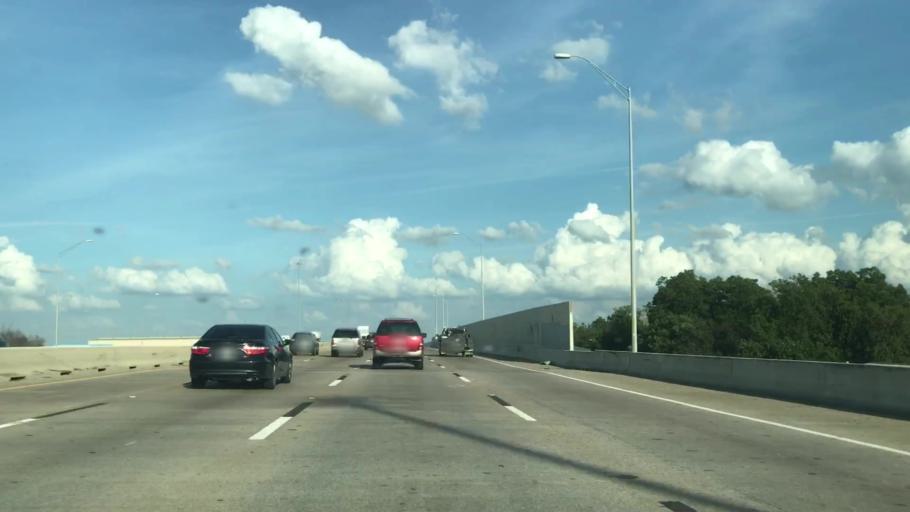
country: US
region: Texas
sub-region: Dallas County
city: Grand Prairie
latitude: 32.7619
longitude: -96.9599
